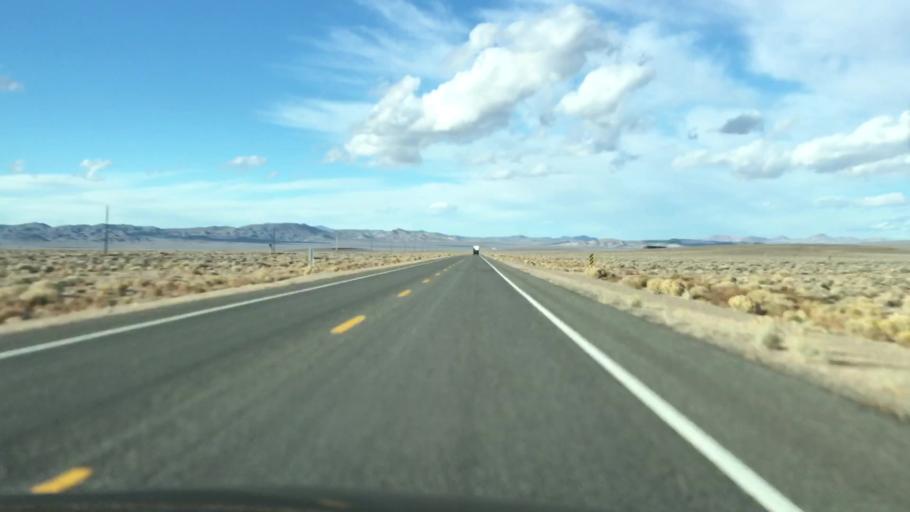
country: US
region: Nevada
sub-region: Esmeralda County
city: Goldfield
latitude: 37.4086
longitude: -117.1519
